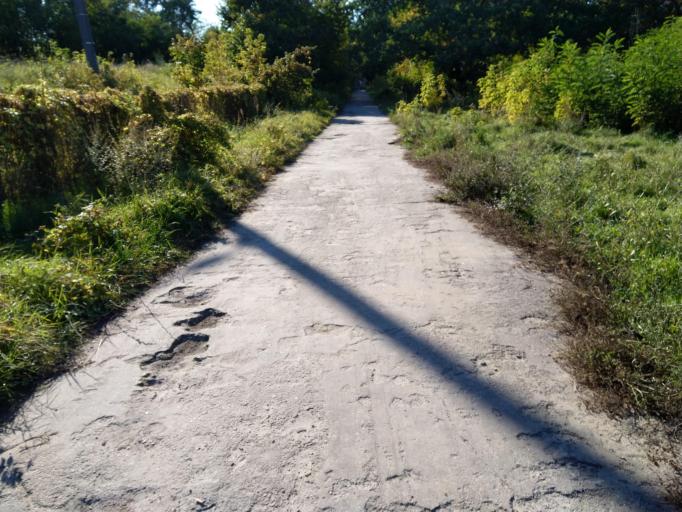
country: DE
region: Berlin
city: Karlshorst
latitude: 52.4953
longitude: 13.5281
